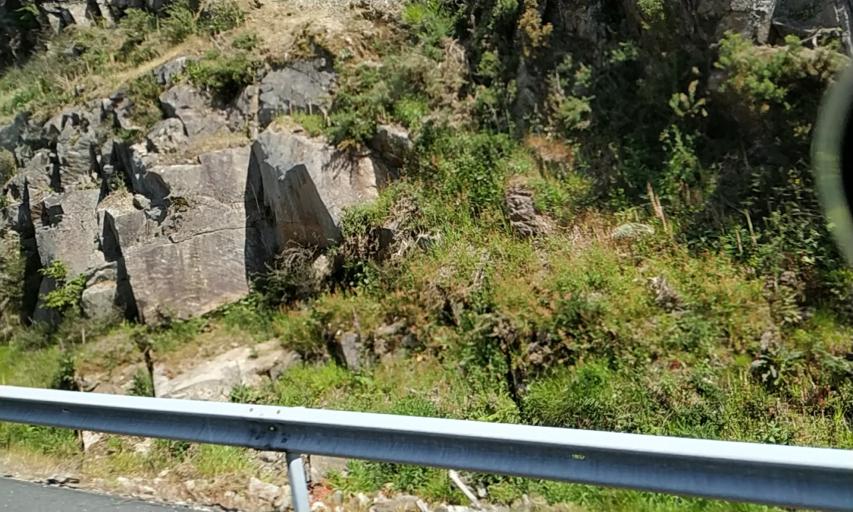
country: ES
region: Galicia
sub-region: Provincia da Coruna
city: Padron
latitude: 42.7814
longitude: -8.6440
